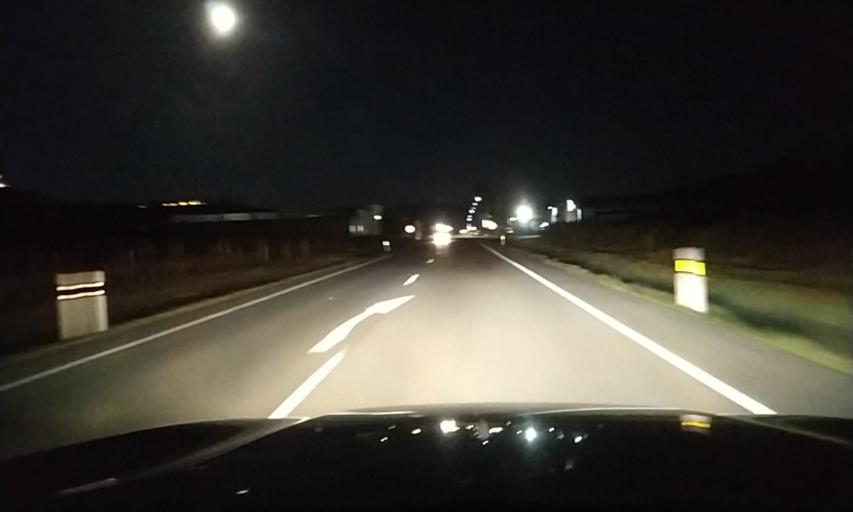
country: ES
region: Galicia
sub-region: Provincia de Ourense
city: Verin
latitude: 41.9424
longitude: -7.4672
